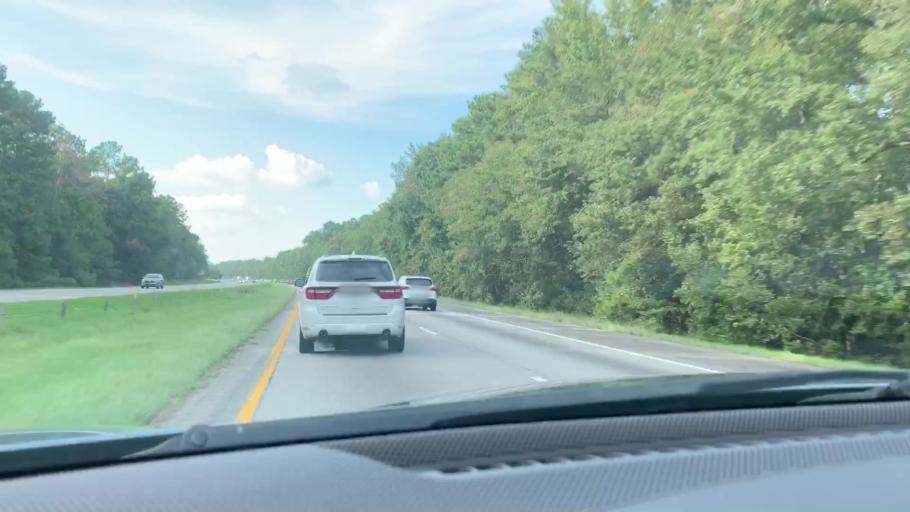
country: US
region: South Carolina
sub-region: Orangeburg County
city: Brookdale
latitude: 33.4953
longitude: -80.7659
